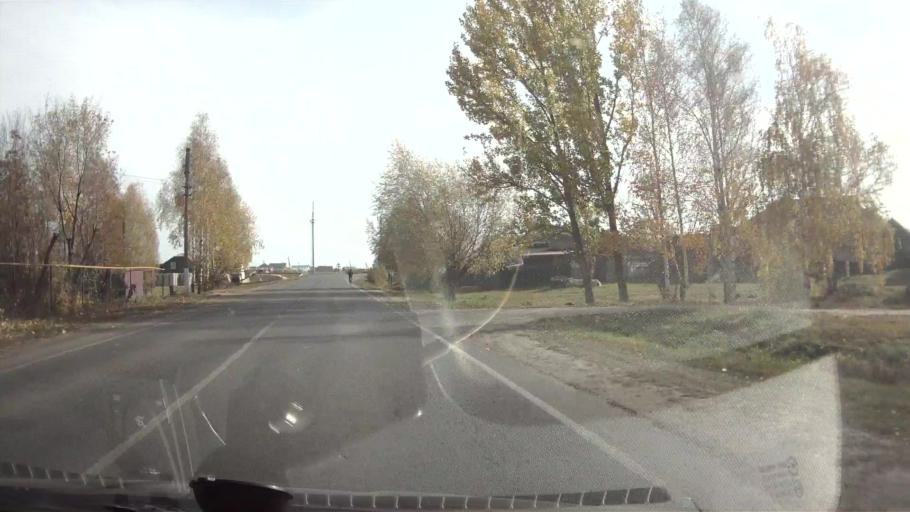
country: RU
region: Mordoviya
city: Turgenevo
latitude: 54.8442
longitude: 46.3496
